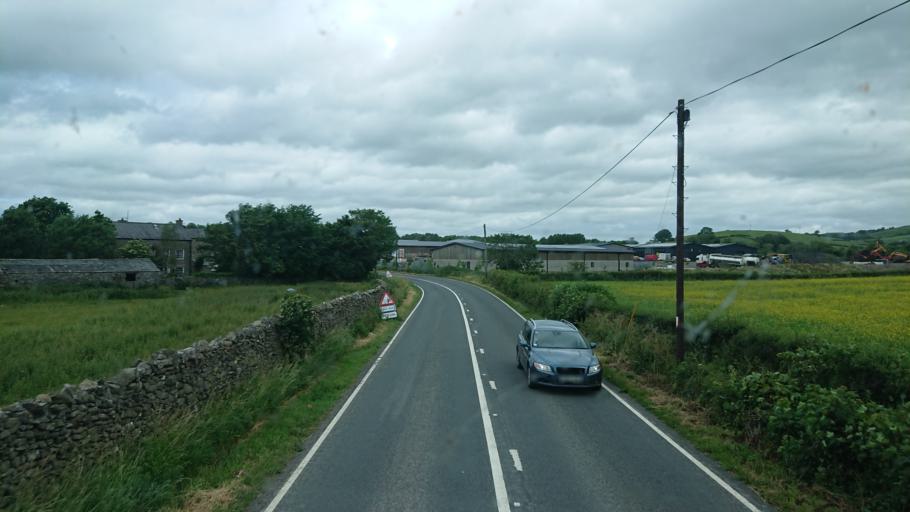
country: GB
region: England
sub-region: Cumbria
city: Milnthorpe
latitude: 54.2308
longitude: -2.7135
